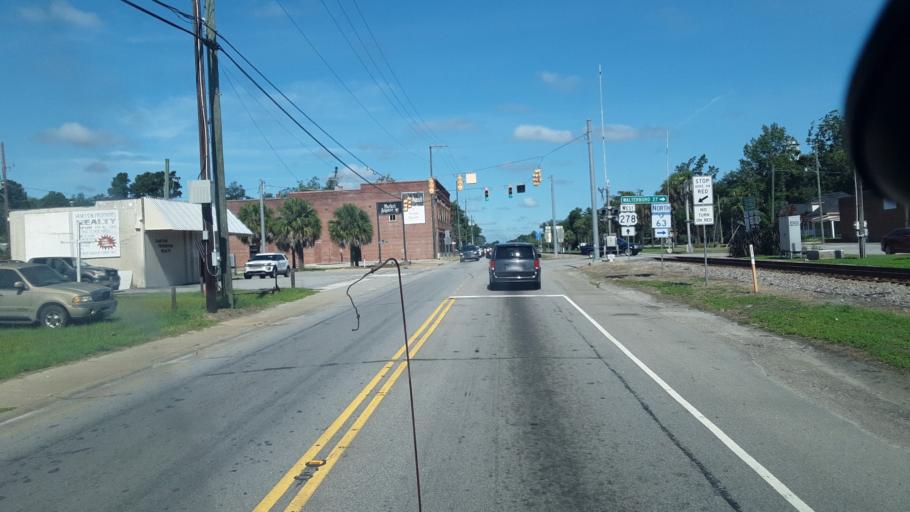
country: US
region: South Carolina
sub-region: Hampton County
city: Varnville
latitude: 32.8499
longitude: -81.0798
